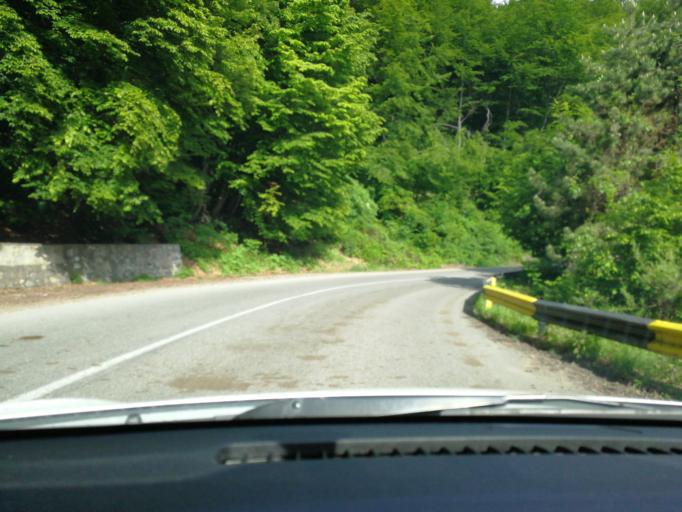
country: RO
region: Prahova
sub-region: Comuna Valea Doftanei
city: Tesila
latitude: 45.2638
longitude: 25.7339
